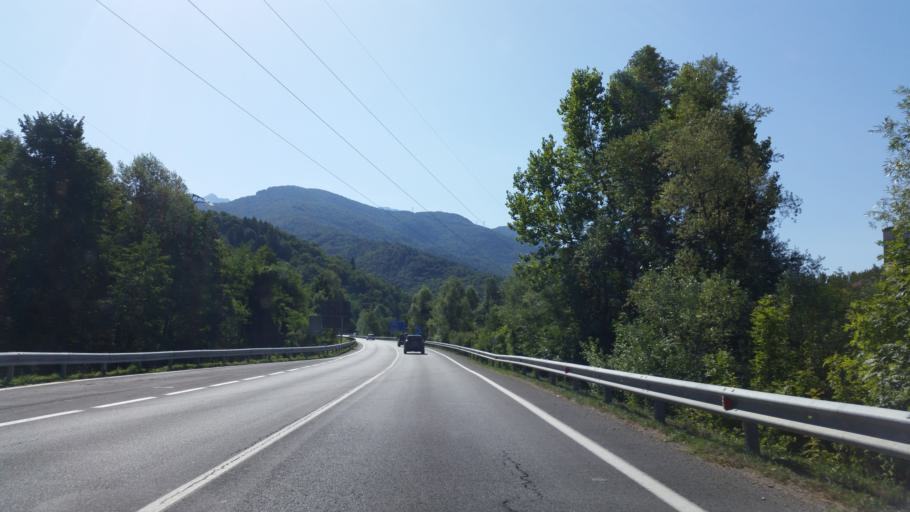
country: IT
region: Piedmont
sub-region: Provincia di Cuneo
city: Robilante
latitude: 44.3051
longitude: 7.5098
